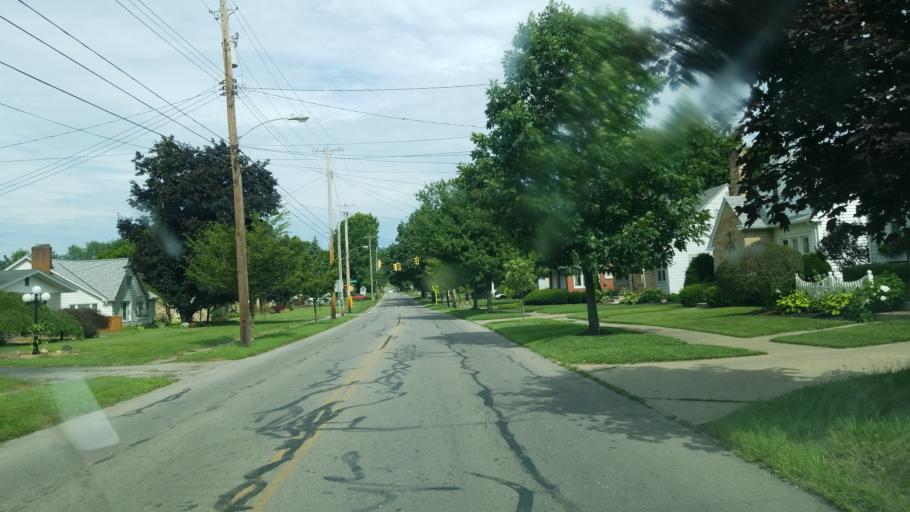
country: US
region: Ohio
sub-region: Ashland County
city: Ashland
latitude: 40.8752
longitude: -82.3284
